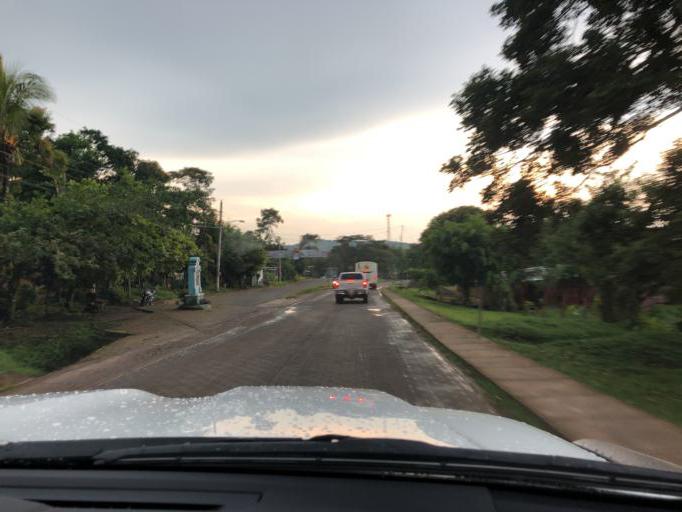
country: NI
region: Chontales
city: La Libertad
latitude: 12.2125
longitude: -85.1732
